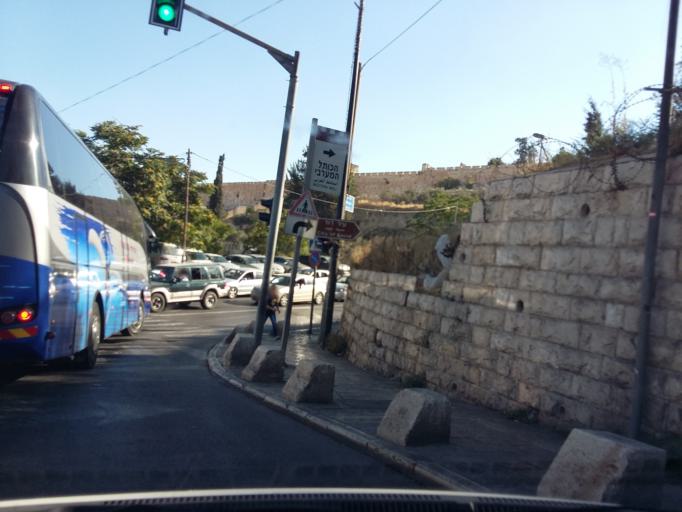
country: PS
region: West Bank
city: East Jerusalem
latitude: 31.7806
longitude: 35.2384
